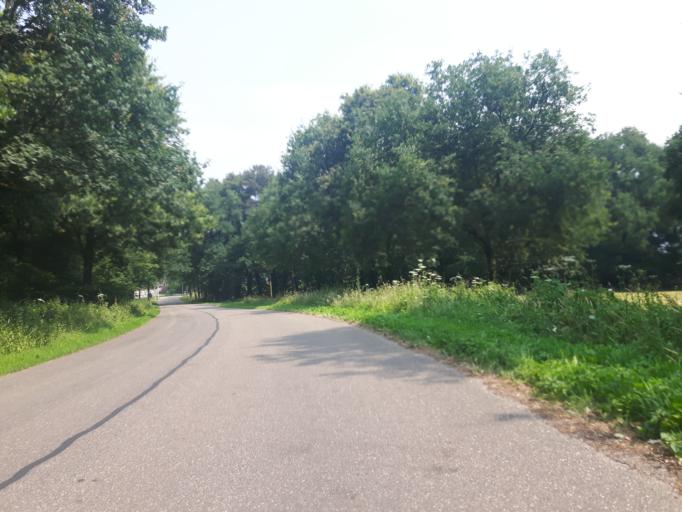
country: NL
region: Overijssel
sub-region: Gemeente Borne
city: Borne
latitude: 52.3054
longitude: 6.7128
